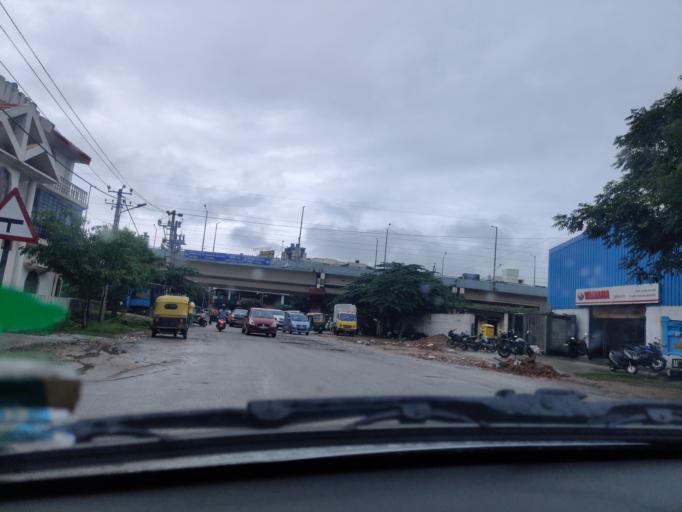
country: IN
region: Karnataka
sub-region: Bangalore Urban
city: Bangalore
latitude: 13.0251
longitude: 77.6435
